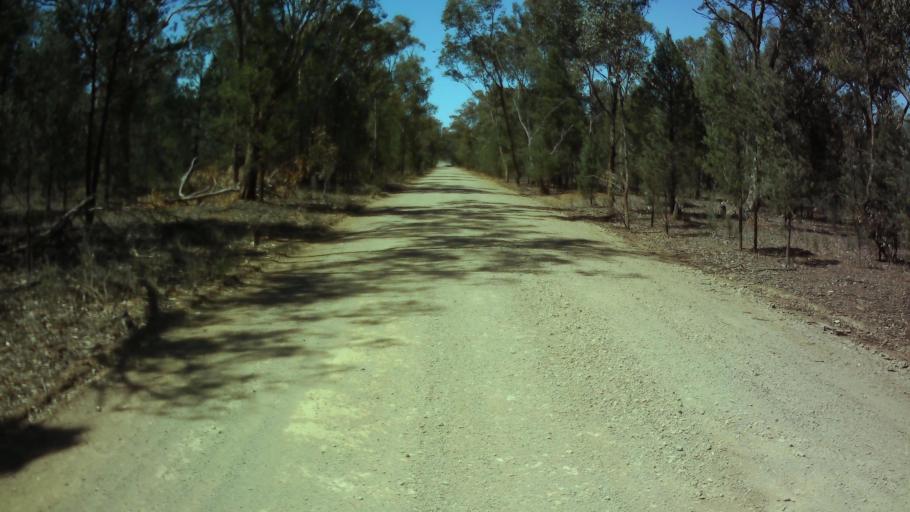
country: AU
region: New South Wales
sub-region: Weddin
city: Grenfell
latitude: -33.8547
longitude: 148.0875
